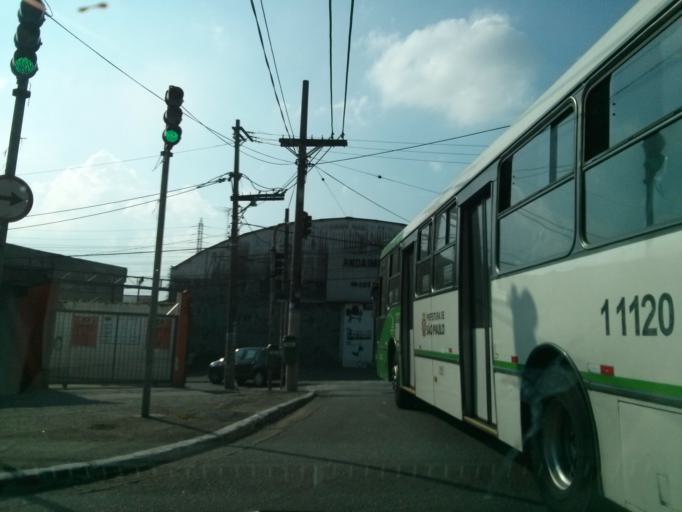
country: BR
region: Sao Paulo
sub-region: Sao Paulo
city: Sao Paulo
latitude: -23.5066
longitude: -46.6666
